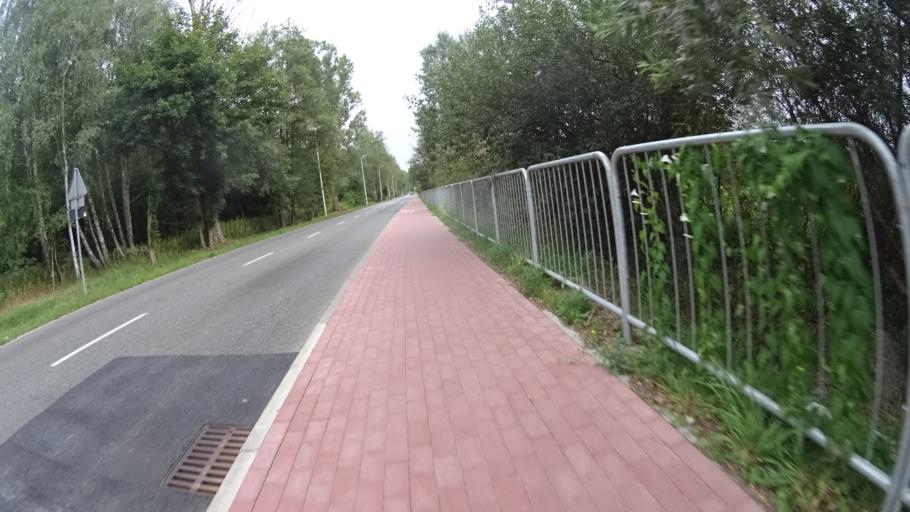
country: PL
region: Masovian Voivodeship
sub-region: Powiat pruszkowski
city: Nadarzyn
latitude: 52.1119
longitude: 20.7993
